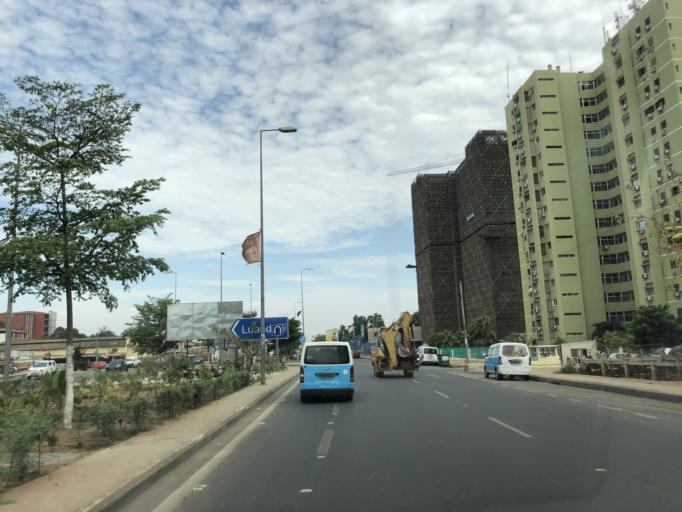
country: AO
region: Luanda
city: Luanda
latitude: -8.8251
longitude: 13.2561
